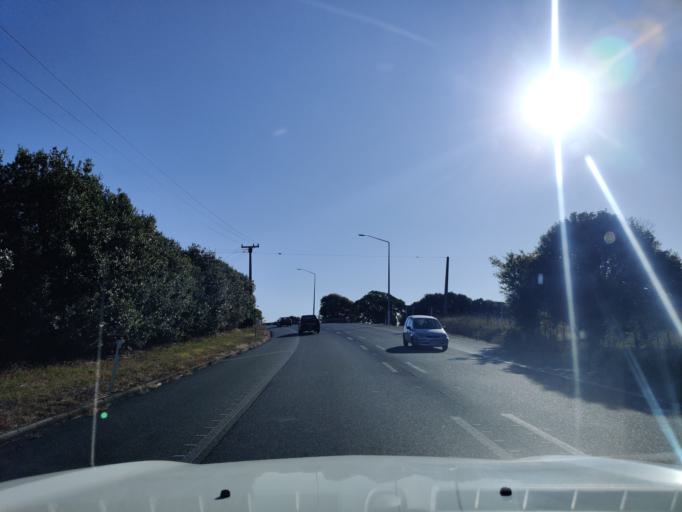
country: NZ
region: Auckland
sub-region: Auckland
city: Papakura
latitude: -37.1194
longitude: 174.9334
